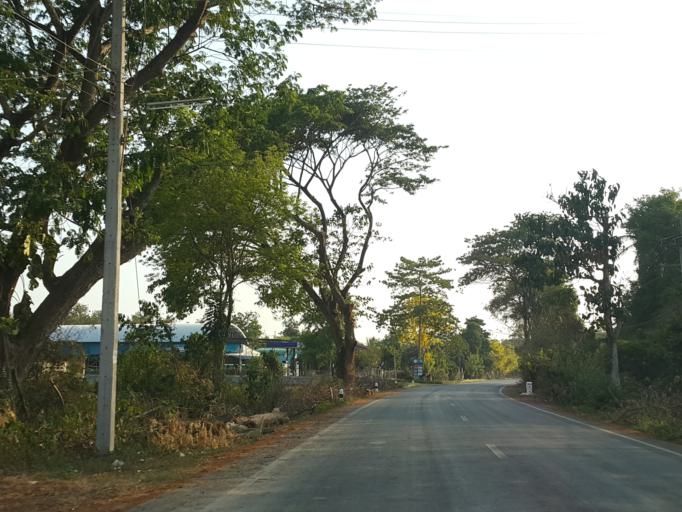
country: TH
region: Uttaradit
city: Phichai
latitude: 17.1680
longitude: 100.1059
